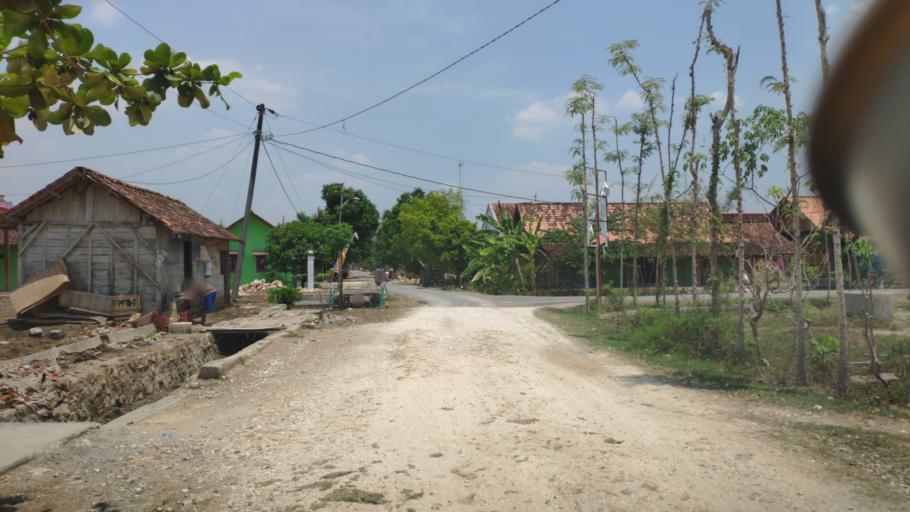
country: ID
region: Central Java
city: Gesik
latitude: -7.0458
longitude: 111.3327
